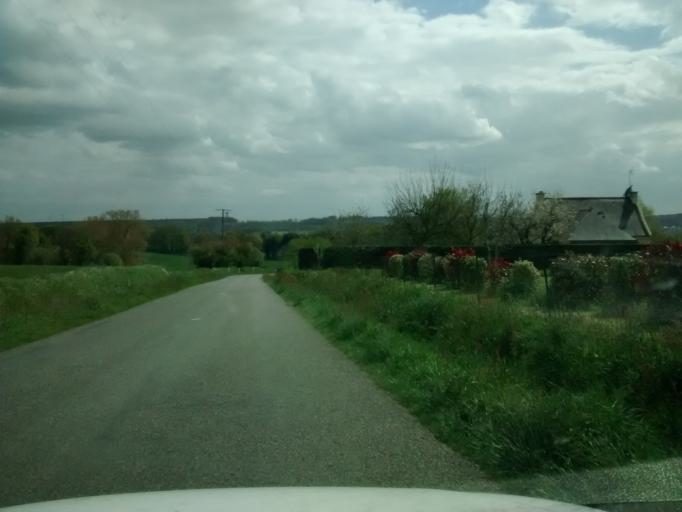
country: FR
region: Brittany
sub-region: Departement du Morbihan
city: Malestroit
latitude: 47.8270
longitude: -2.3650
